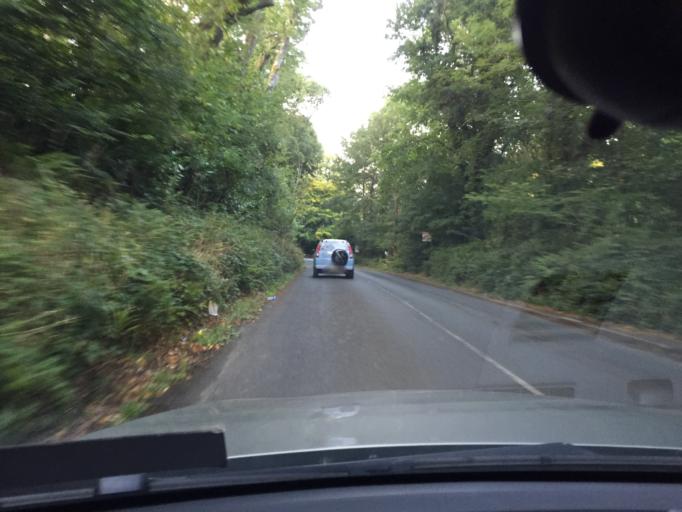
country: IE
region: Leinster
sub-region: Wicklow
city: Enniskerry
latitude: 53.1803
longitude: -6.1721
